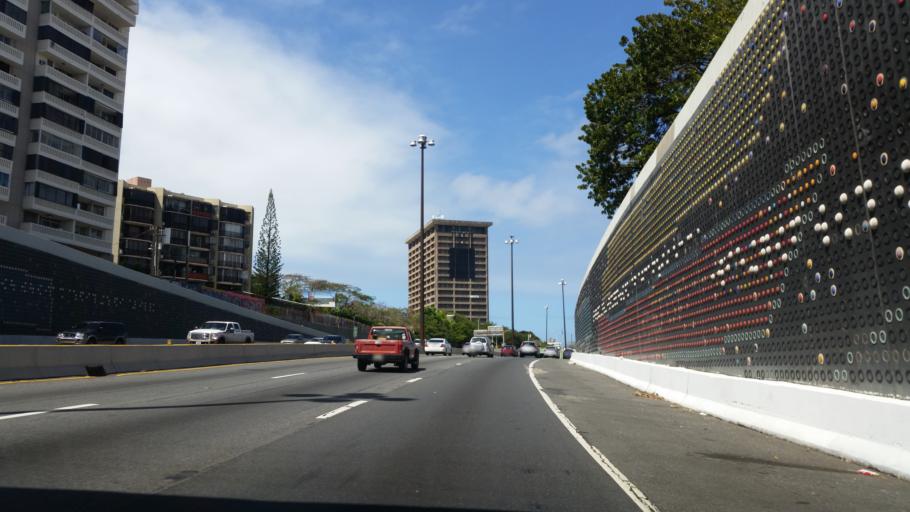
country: PR
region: San Juan
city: San Juan
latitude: 18.4486
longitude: -66.0635
